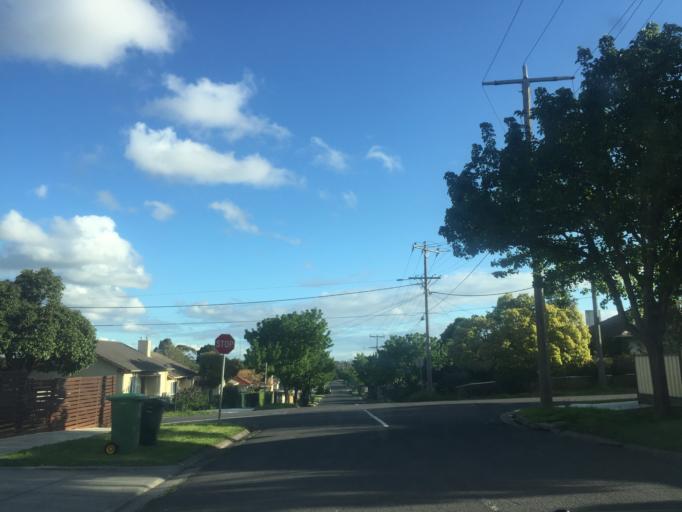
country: AU
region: Victoria
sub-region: Darebin
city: Kingsbury
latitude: -37.7270
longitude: 145.0348
